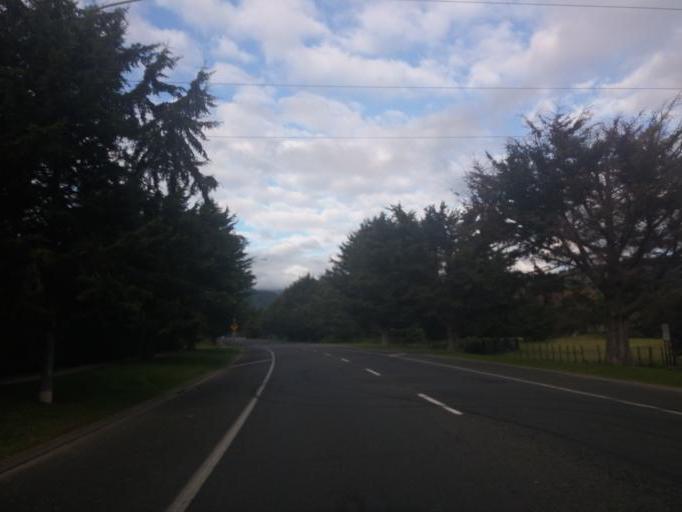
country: NZ
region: Wellington
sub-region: Kapiti Coast District
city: Paraparaumu
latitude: -40.8743
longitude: 175.0480
